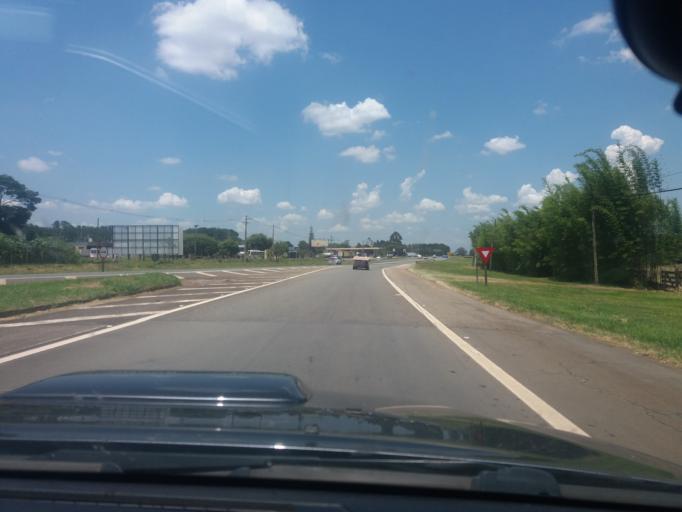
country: BR
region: Sao Paulo
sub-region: Itapetininga
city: Itapetininga
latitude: -23.5927
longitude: -47.9889
